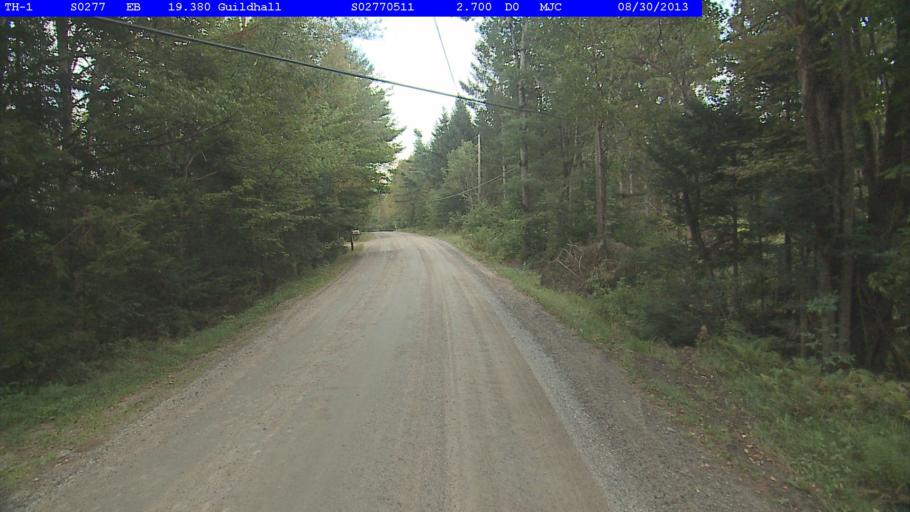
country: US
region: Vermont
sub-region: Essex County
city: Guildhall
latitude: 44.5578
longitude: -71.6231
